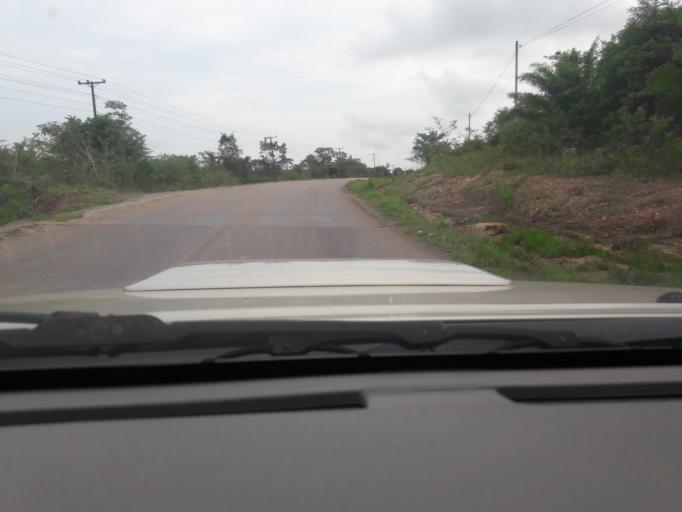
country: TH
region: Nong Khai
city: Rattanawapi
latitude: 18.2512
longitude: 103.1484
